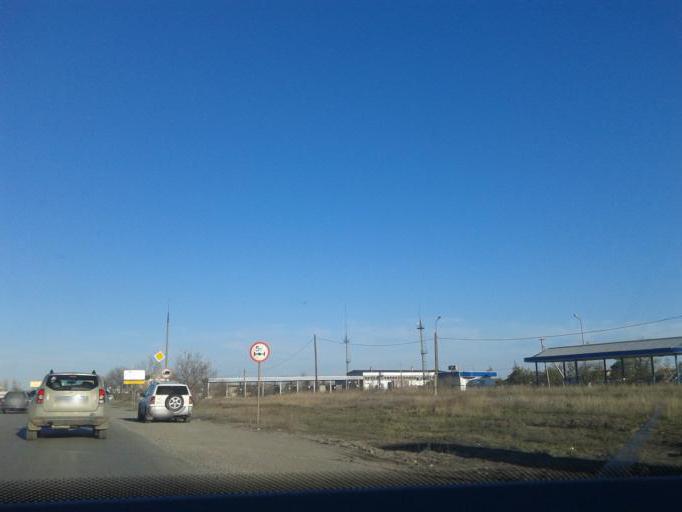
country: RU
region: Volgograd
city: Volgograd
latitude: 48.7044
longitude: 44.4423
